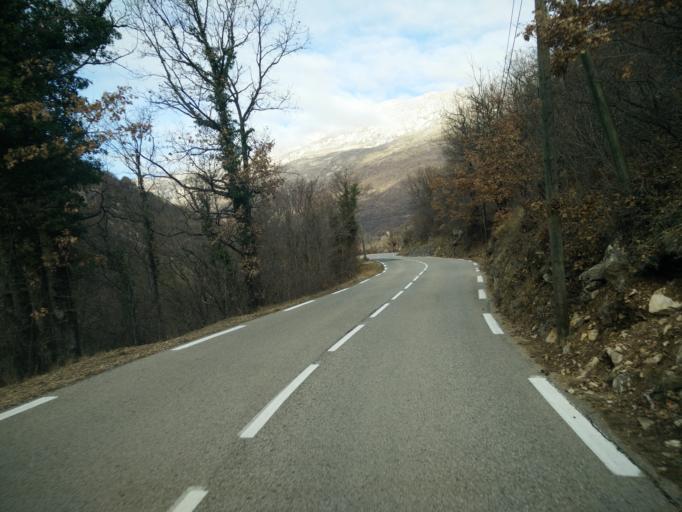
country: FR
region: Provence-Alpes-Cote d'Azur
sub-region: Departement des Alpes-Maritimes
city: Tourrettes-sur-Loup
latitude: 43.7821
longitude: 6.9768
